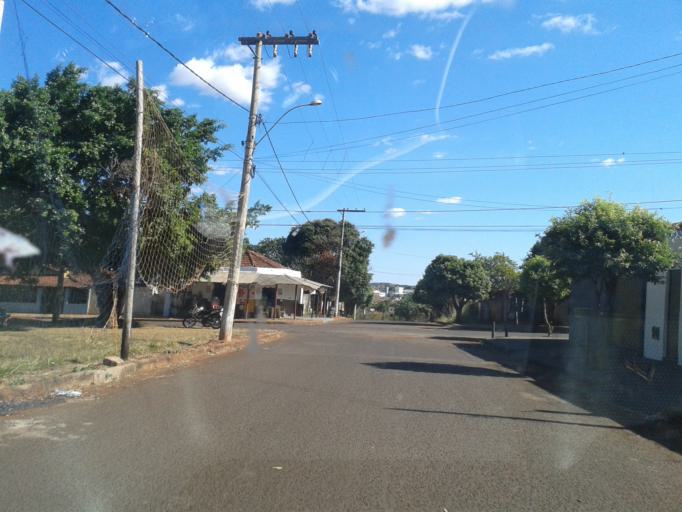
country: BR
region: Minas Gerais
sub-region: Ituiutaba
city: Ituiutaba
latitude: -18.9586
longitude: -49.4602
